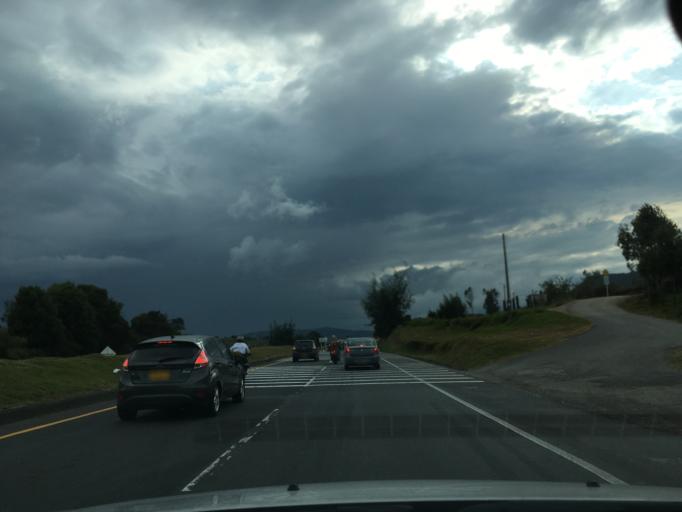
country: CO
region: Boyaca
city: Ventaquemada
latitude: 5.4028
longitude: -73.4789
